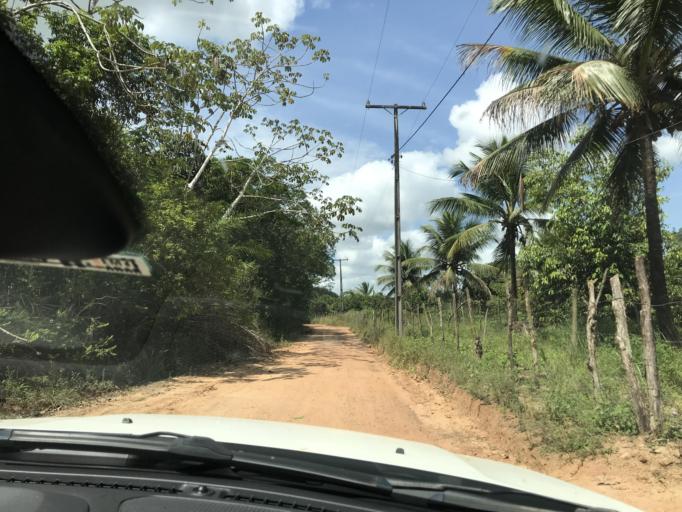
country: BR
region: Bahia
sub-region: Entre Rios
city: Entre Rios
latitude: -12.2190
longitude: -38.0822
